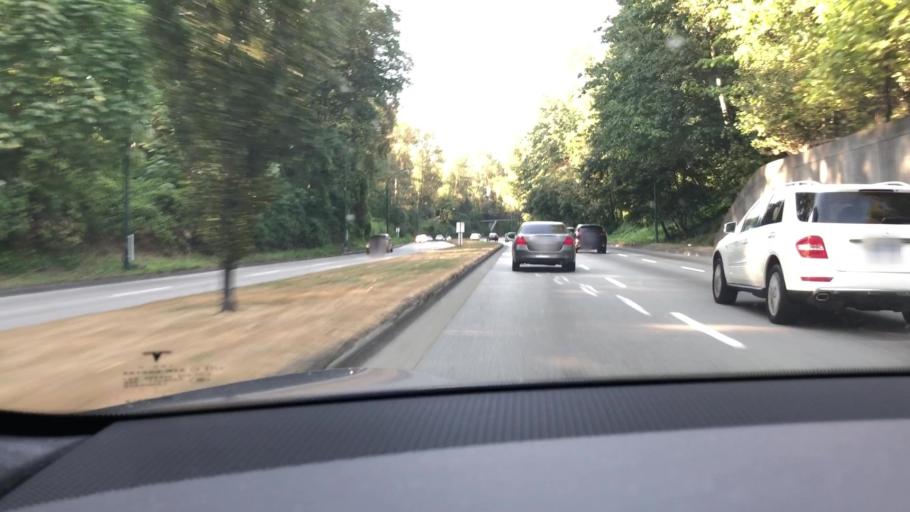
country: CA
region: British Columbia
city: Burnaby
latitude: 49.2085
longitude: -123.0236
